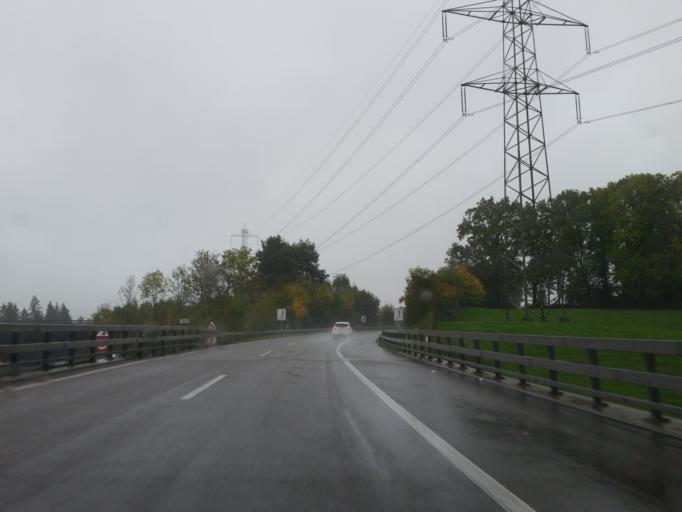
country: CH
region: Saint Gallen
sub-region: Wahlkreis Rorschach
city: Morschwil
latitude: 47.4699
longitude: 9.4427
